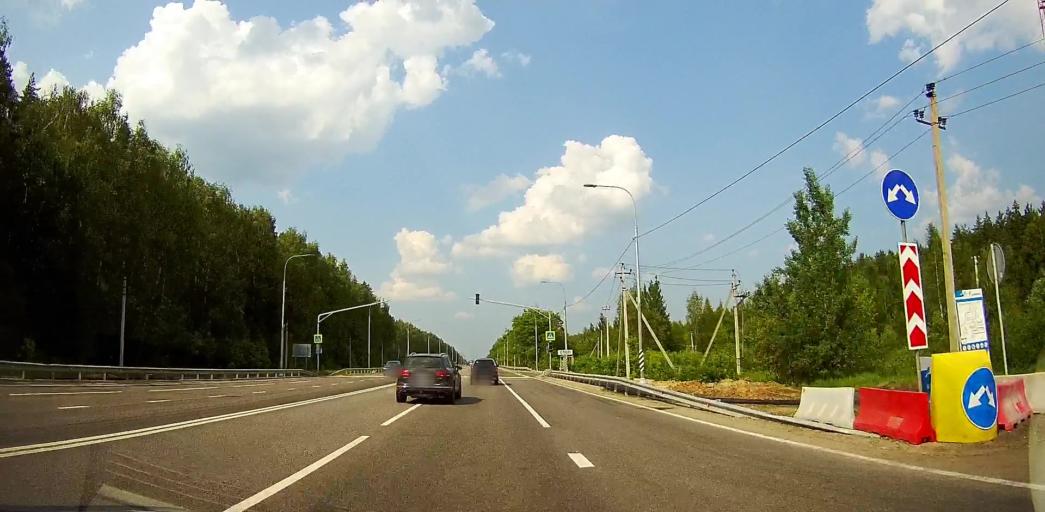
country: RU
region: Moskovskaya
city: Mikhnevo
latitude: 55.0782
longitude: 37.9525
